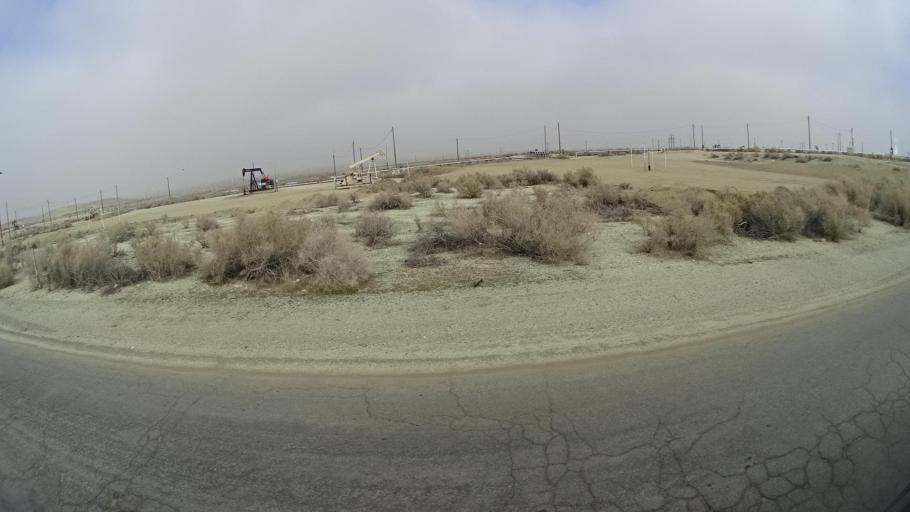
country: US
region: California
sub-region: Kern County
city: Maricopa
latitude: 35.0340
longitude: -119.3514
